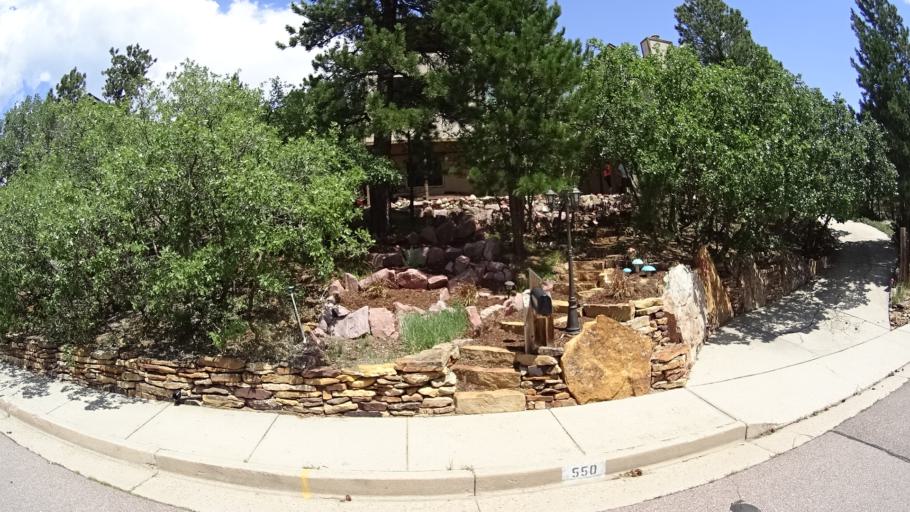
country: US
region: Colorado
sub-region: El Paso County
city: Air Force Academy
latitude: 38.9393
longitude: -104.8381
